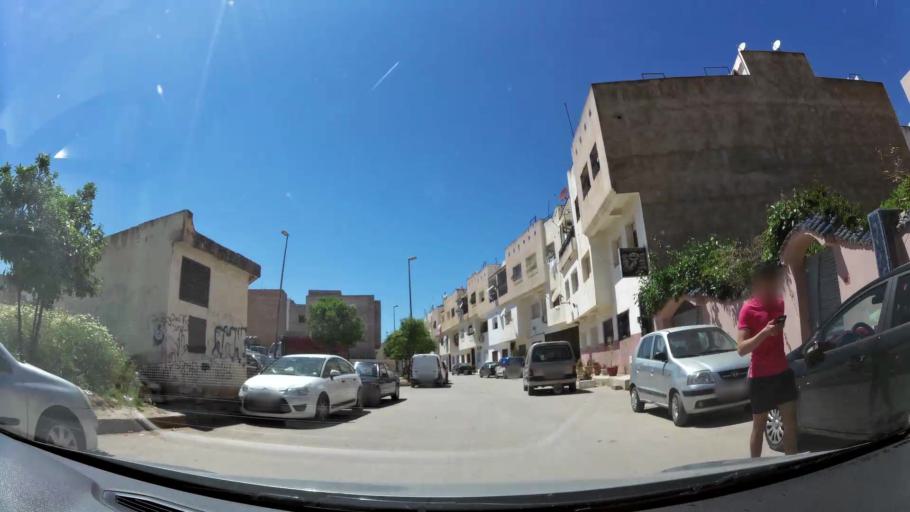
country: MA
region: Fes-Boulemane
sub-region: Fes
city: Fes
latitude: 34.0189
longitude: -5.0049
